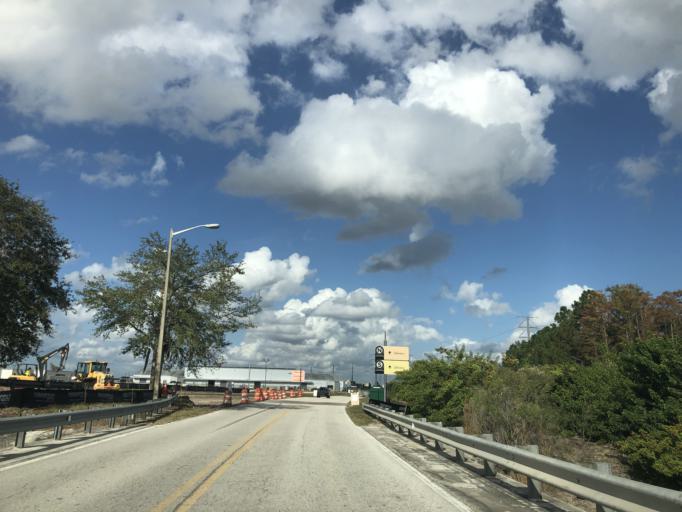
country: US
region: Florida
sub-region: Orange County
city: Williamsburg
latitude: 28.4258
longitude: -81.4550
